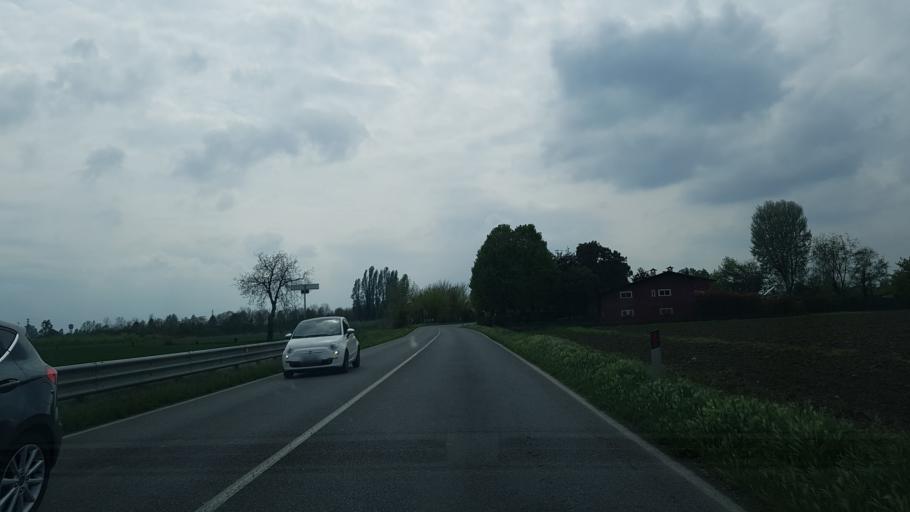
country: IT
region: Veneto
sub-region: Provincia di Verona
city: Minerbe
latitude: 45.2204
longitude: 11.3242
